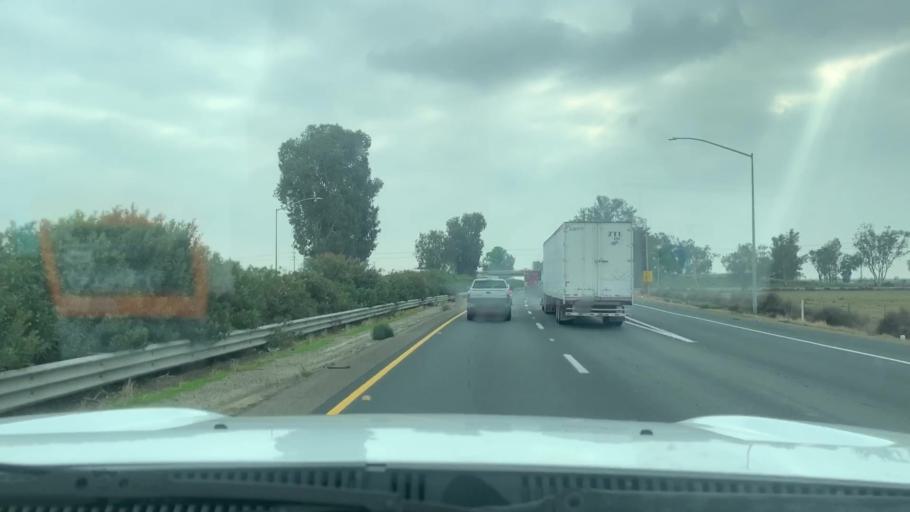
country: US
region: California
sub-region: Tulare County
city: Tipton
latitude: 36.0540
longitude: -119.3111
